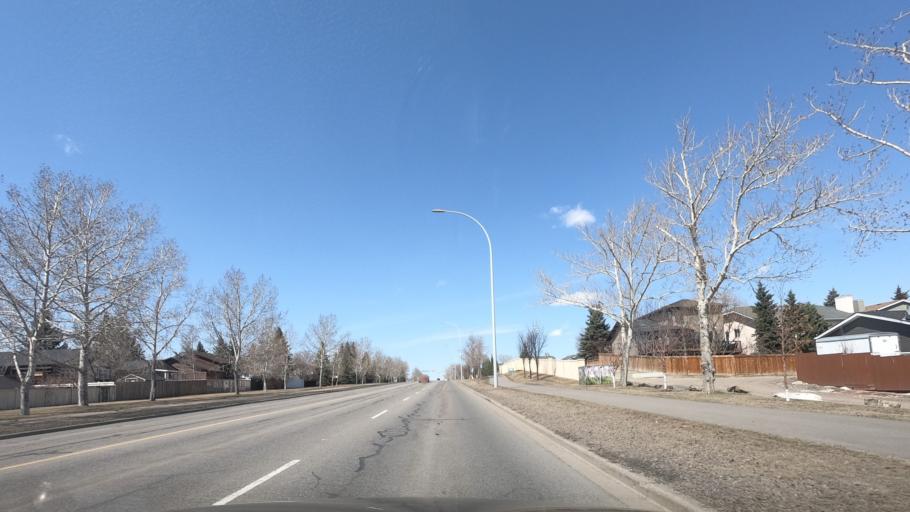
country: CA
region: Alberta
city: Airdrie
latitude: 51.2777
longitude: -113.9898
